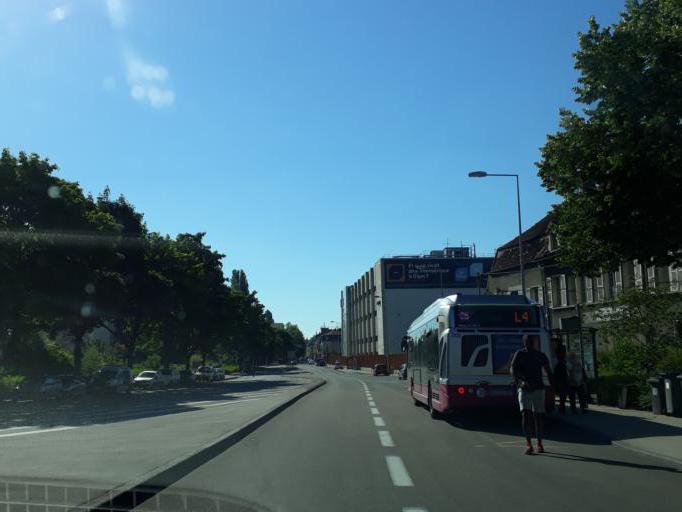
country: FR
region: Bourgogne
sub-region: Departement de la Cote-d'Or
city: Dijon
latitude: 47.3180
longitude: 5.0313
